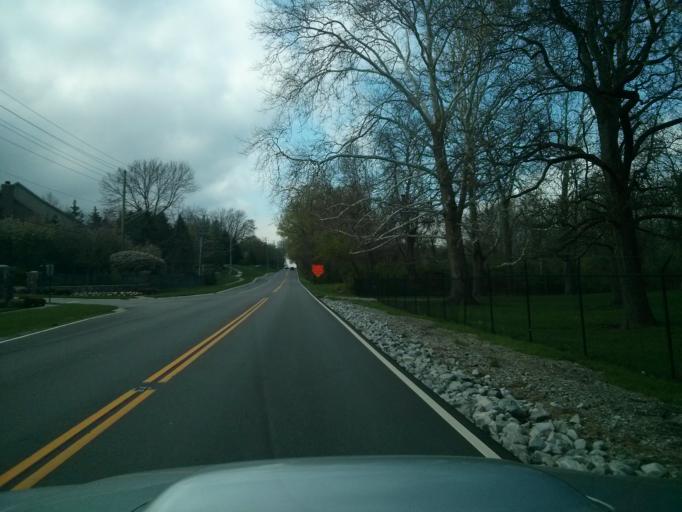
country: US
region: Indiana
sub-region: Marion County
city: Meridian Hills
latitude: 39.9389
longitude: -86.1651
